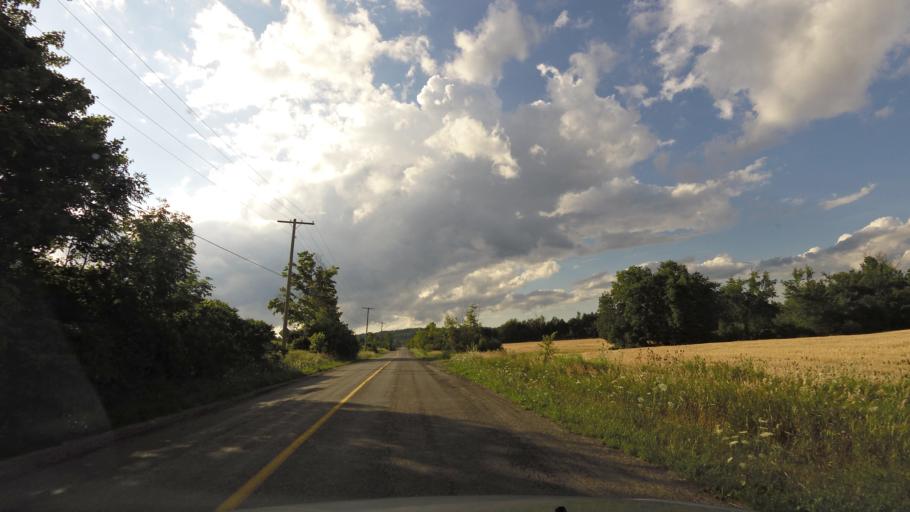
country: CA
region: Ontario
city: Brampton
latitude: 43.7607
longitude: -79.9333
